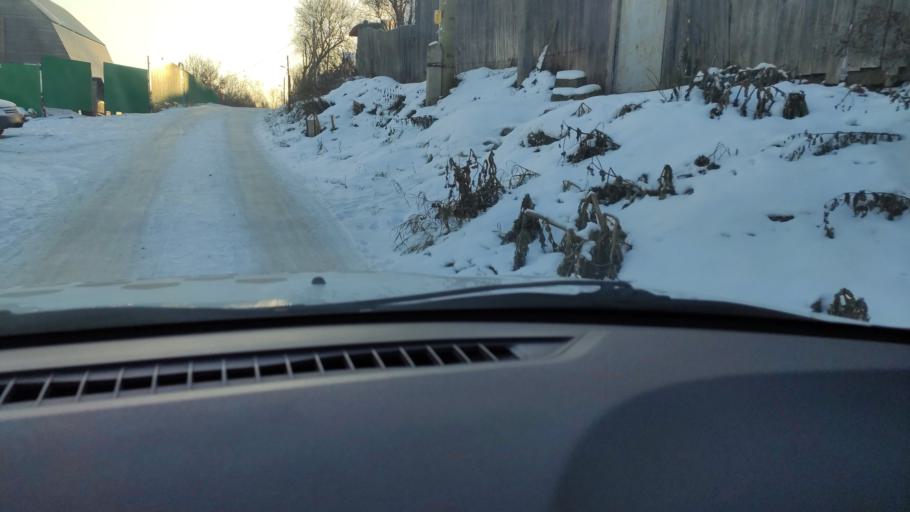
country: RU
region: Perm
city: Perm
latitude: 58.0340
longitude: 56.3308
